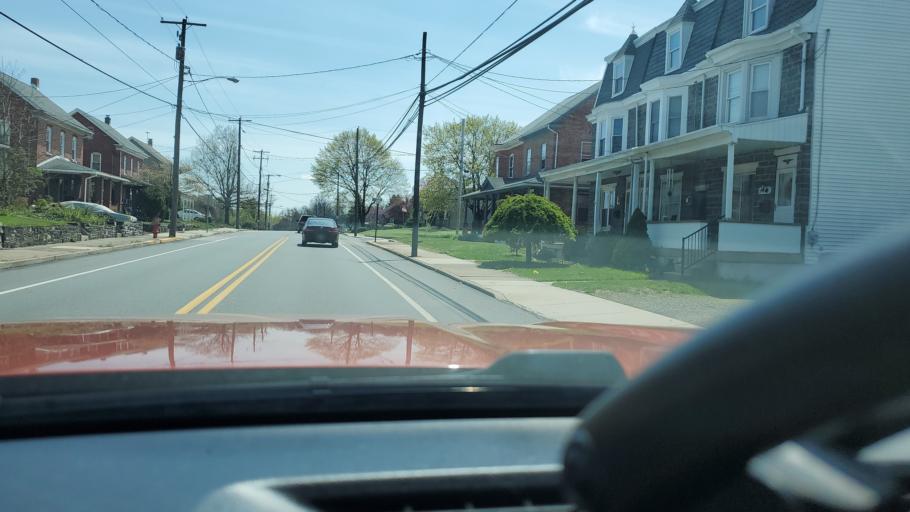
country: US
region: Pennsylvania
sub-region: Montgomery County
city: Red Hill
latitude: 40.3694
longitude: -75.4831
